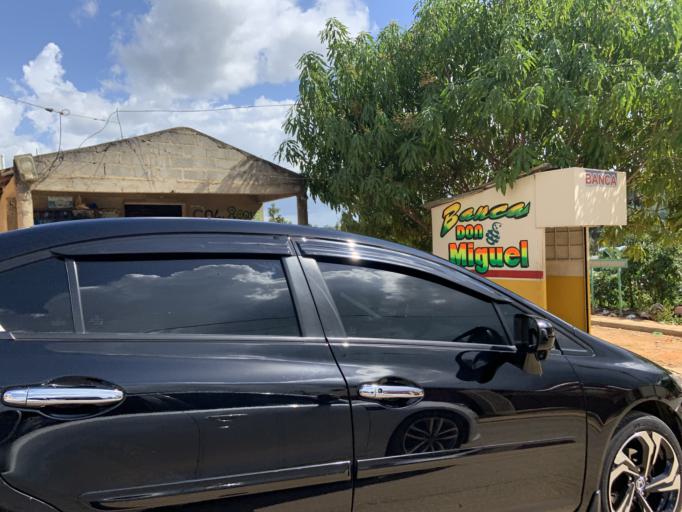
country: DO
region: Monte Plata
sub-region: Yamasa
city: Yamasa
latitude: 18.7685
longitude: -70.0298
